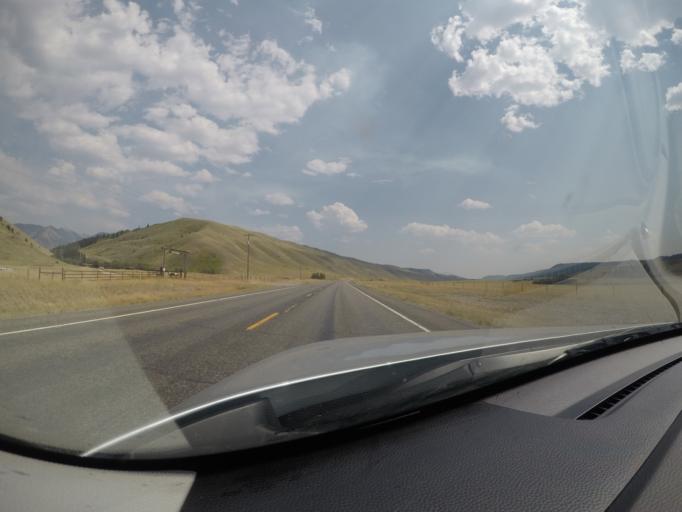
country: US
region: Montana
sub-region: Gallatin County
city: Big Sky
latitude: 44.9618
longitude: -111.6287
